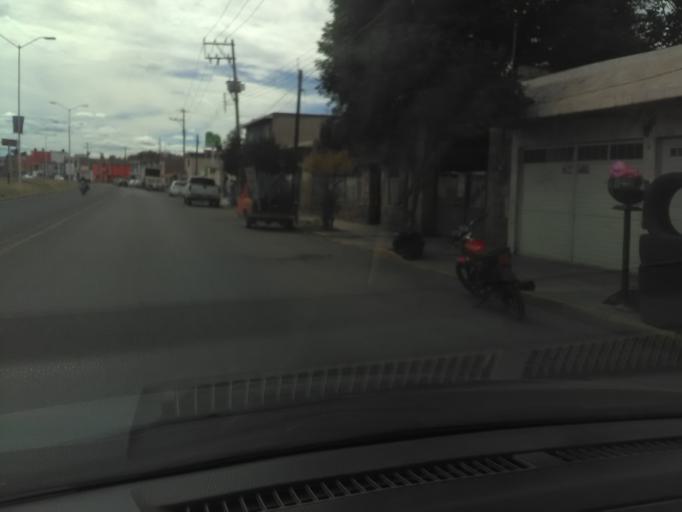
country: MX
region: Durango
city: Victoria de Durango
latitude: 24.0410
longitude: -104.6801
